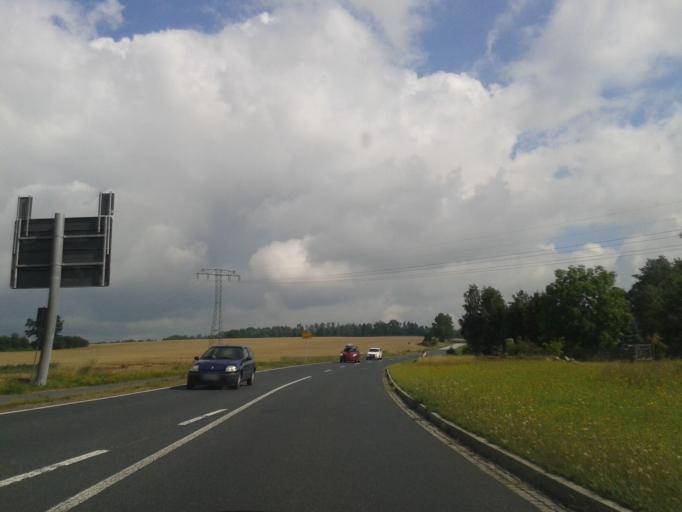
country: DE
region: Saxony
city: Radeberg
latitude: 51.1256
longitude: 13.9373
